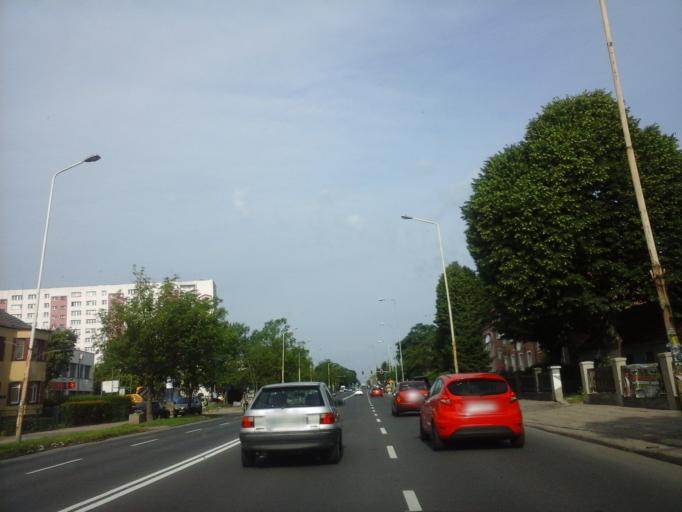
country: PL
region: West Pomeranian Voivodeship
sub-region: Powiat stargardzki
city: Stargard Szczecinski
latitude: 53.3404
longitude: 15.0146
